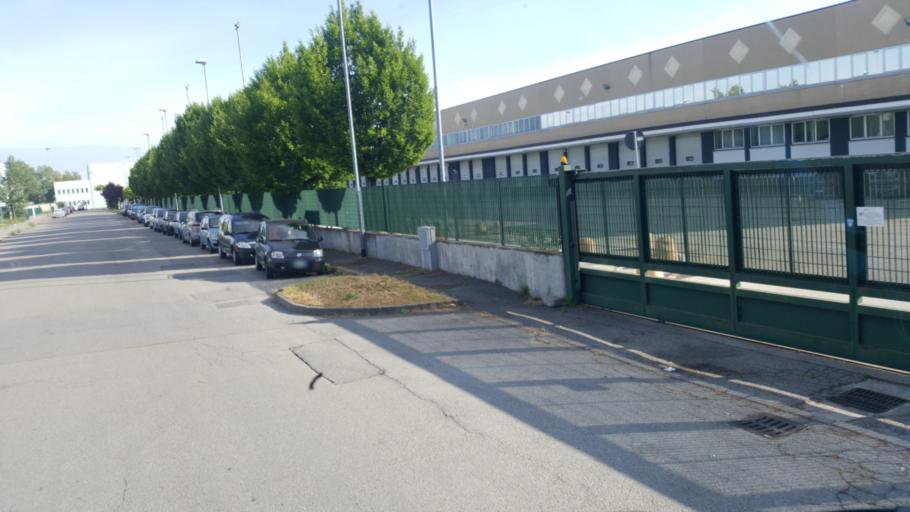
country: IT
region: Lombardy
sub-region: Citta metropolitana di Milano
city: Liscate
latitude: 45.4874
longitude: 9.4126
